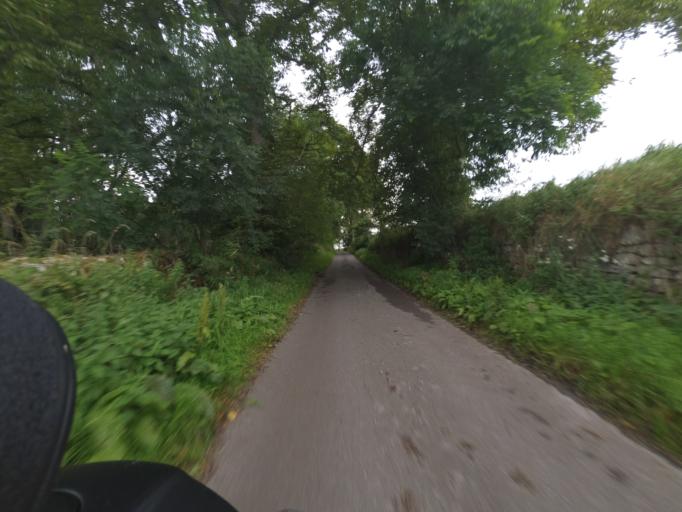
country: GB
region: Scotland
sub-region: Highland
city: Conon Bridge
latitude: 57.5138
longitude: -4.3715
